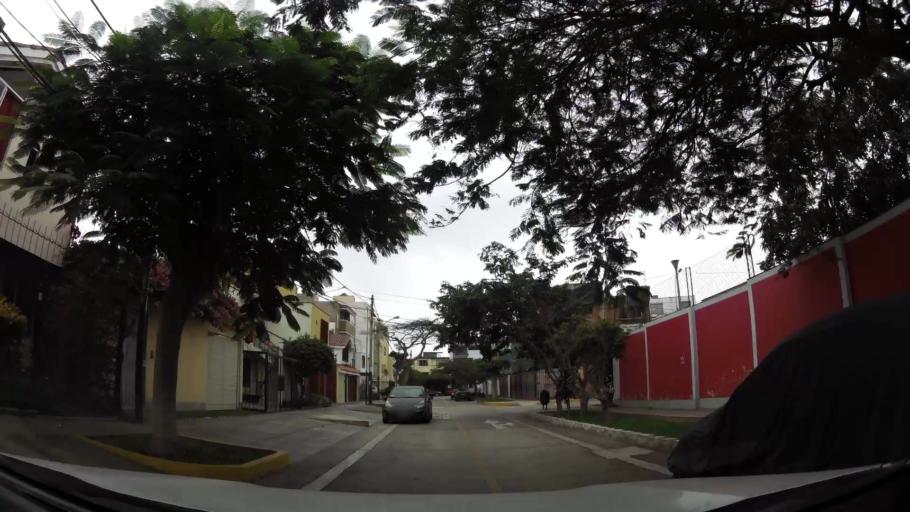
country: PE
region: Lima
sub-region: Lima
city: Surco
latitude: -12.1383
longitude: -76.9897
